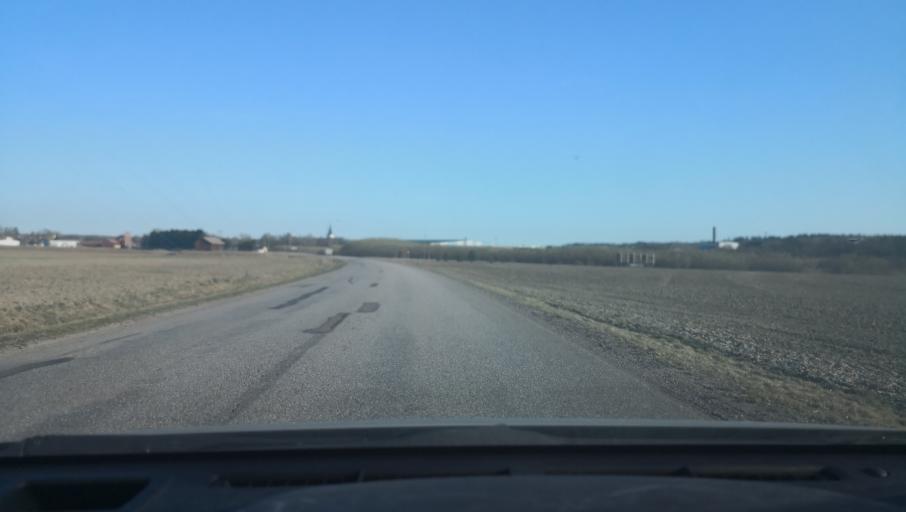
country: SE
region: Uppsala
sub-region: Heby Kommun
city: Heby
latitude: 59.9501
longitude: 16.8408
